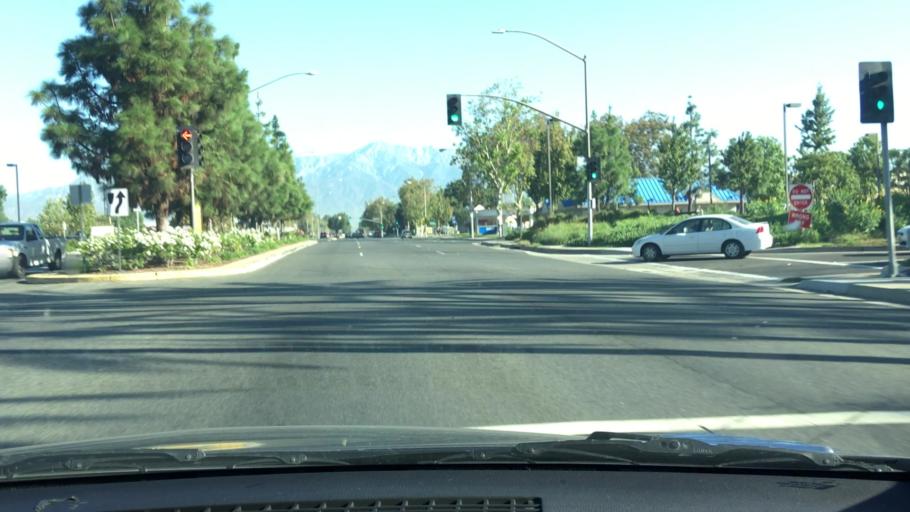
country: US
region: California
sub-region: San Bernardino County
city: Ontario
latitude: 34.0311
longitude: -117.5931
